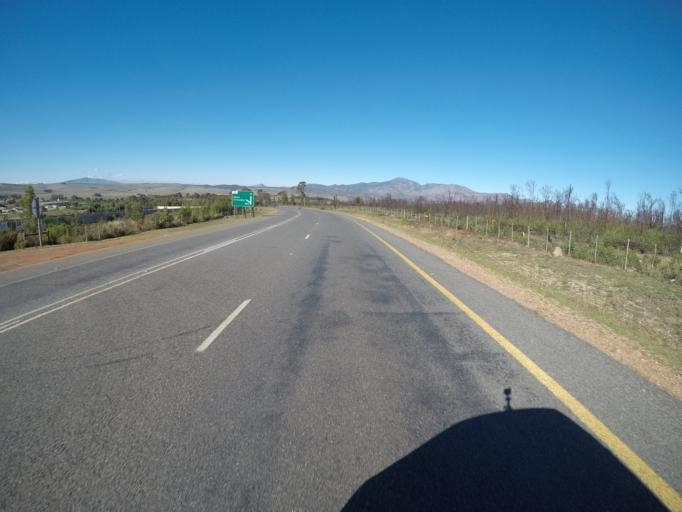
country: ZA
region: Western Cape
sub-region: Overberg District Municipality
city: Hermanus
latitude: -34.2340
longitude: 19.1904
